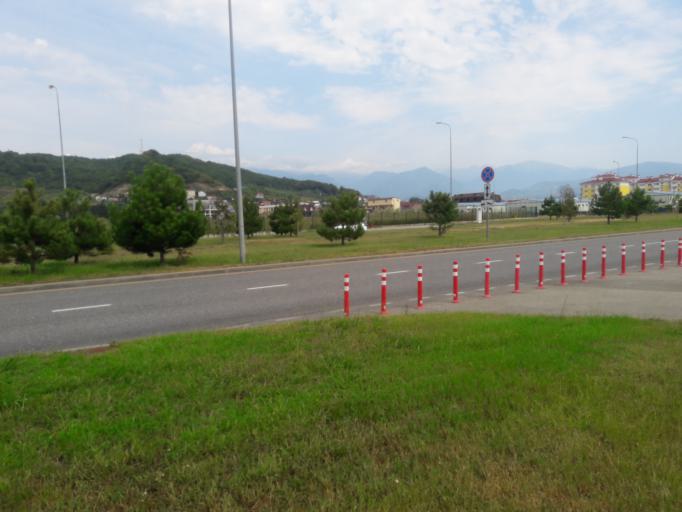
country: RU
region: Krasnodarskiy
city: Adler
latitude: 43.4040
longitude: 39.9784
